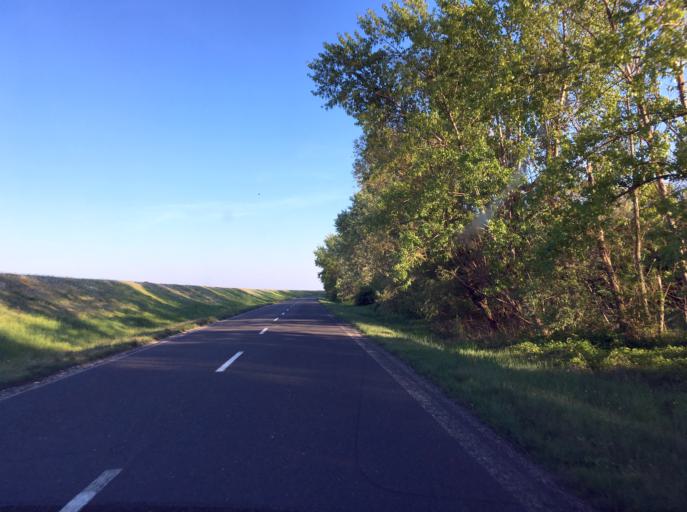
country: HU
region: Gyor-Moson-Sopron
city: Rajka
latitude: 48.0290
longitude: 17.2395
